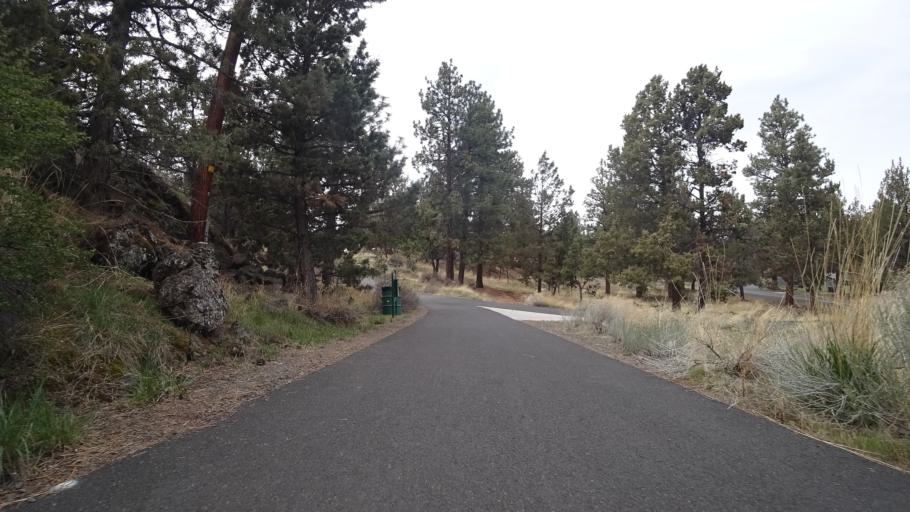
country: US
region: Oregon
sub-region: Deschutes County
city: Bend
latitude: 44.0514
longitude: -121.2905
